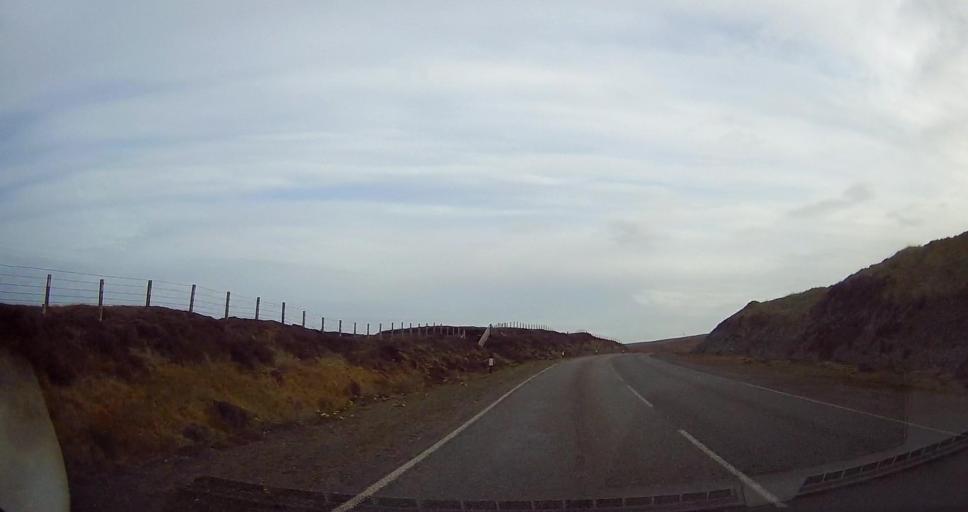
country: GB
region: Scotland
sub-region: Shetland Islands
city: Sandwick
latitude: 60.0900
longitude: -1.2284
